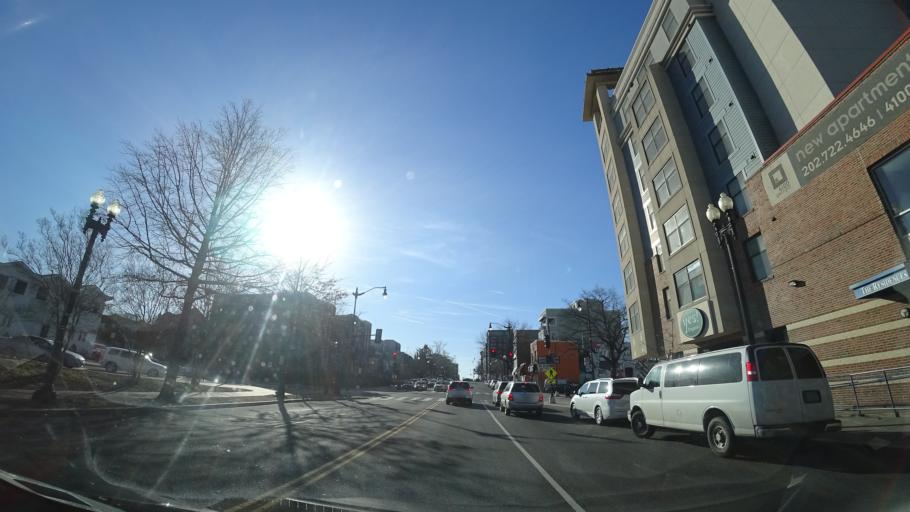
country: US
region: Maryland
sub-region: Montgomery County
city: Takoma Park
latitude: 38.9412
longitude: -77.0254
